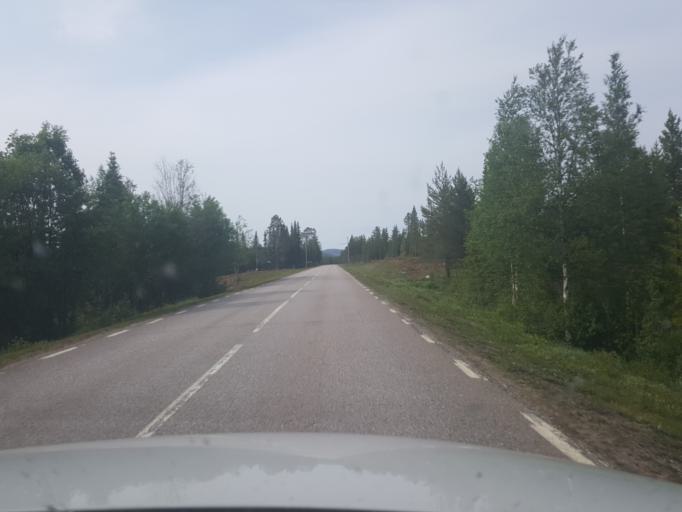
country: SE
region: Norrbotten
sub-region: Arjeplogs Kommun
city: Arjeplog
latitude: 65.7689
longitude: 18.0195
